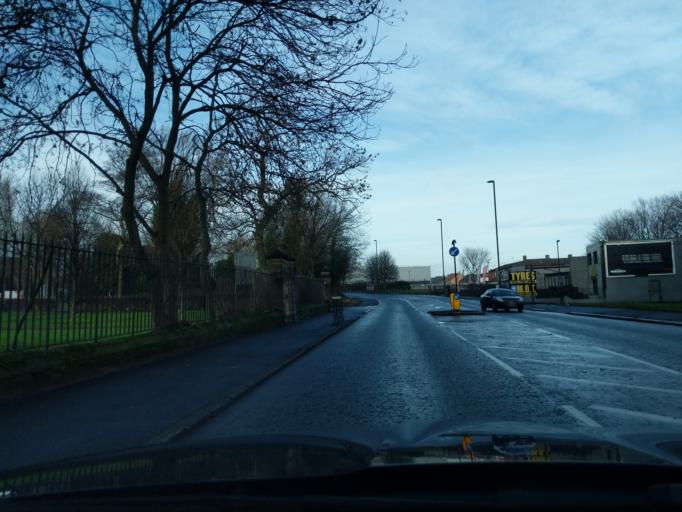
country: GB
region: England
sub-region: Gateshead
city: Felling
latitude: 54.9751
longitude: -1.5708
